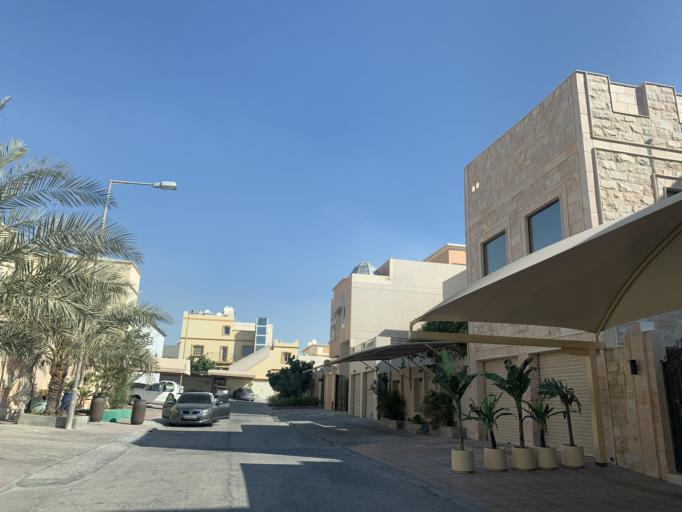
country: BH
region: Central Governorate
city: Madinat Hamad
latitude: 26.1195
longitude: 50.5050
